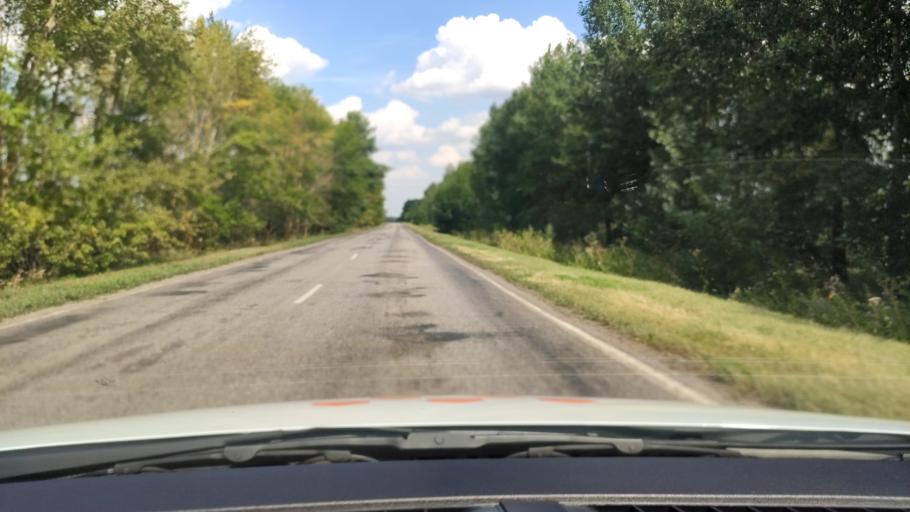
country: RU
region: Voronezj
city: Pereleshinskiy
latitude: 51.7221
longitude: 40.3600
